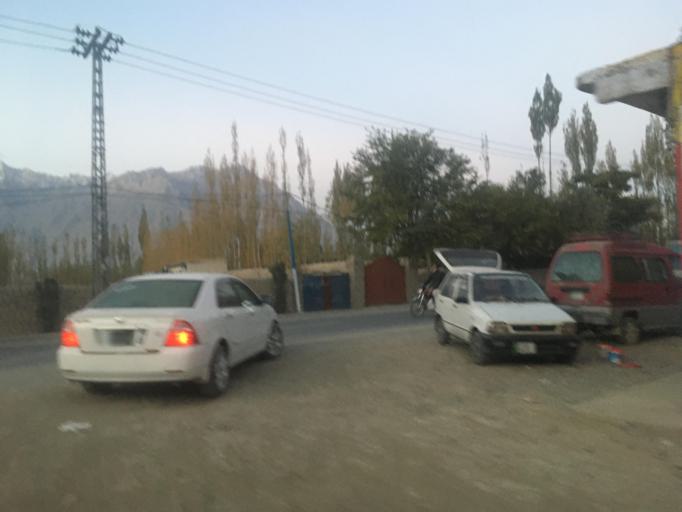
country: PK
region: Gilgit-Baltistan
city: Skardu
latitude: 35.2949
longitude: 75.5699
